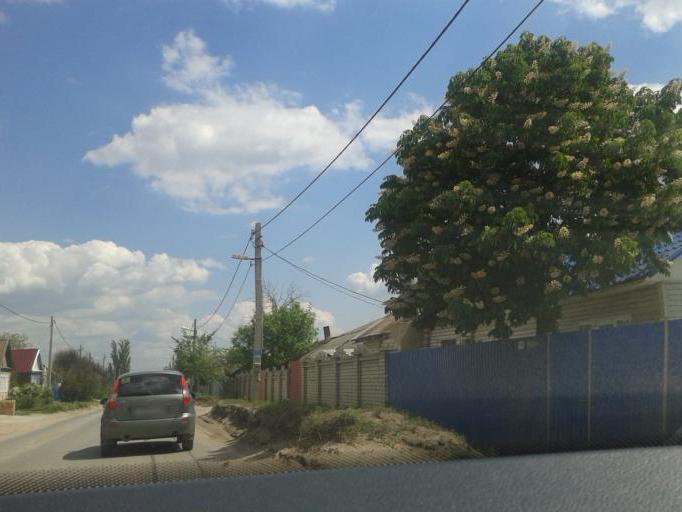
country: RU
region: Volgograd
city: Volgograd
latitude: 48.6909
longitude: 44.4554
